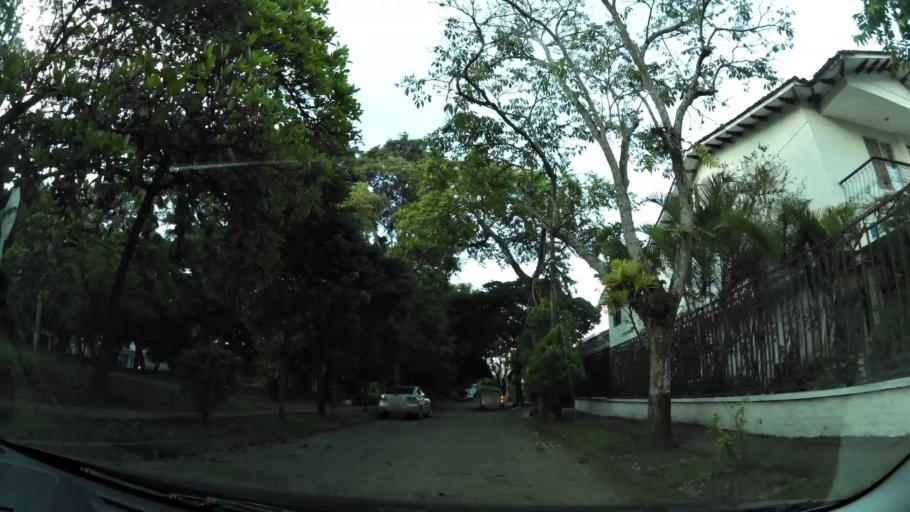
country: CO
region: Valle del Cauca
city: Cali
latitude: 3.4051
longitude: -76.5542
